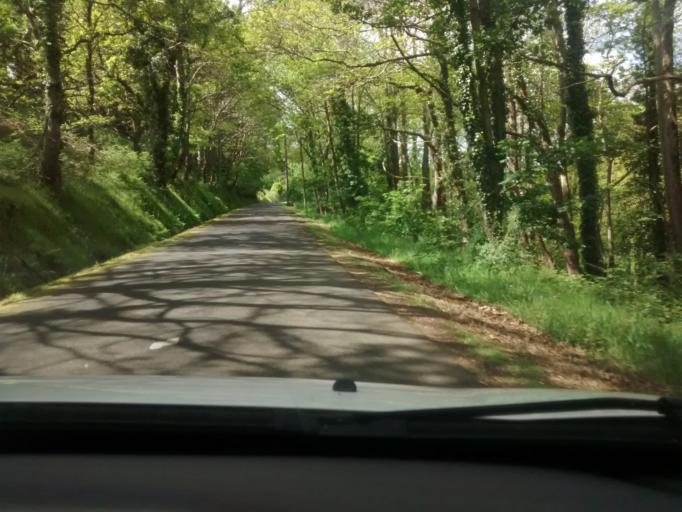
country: FR
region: Brittany
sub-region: Departement des Cotes-d'Armor
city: Louannec
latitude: 48.7996
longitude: -3.4010
